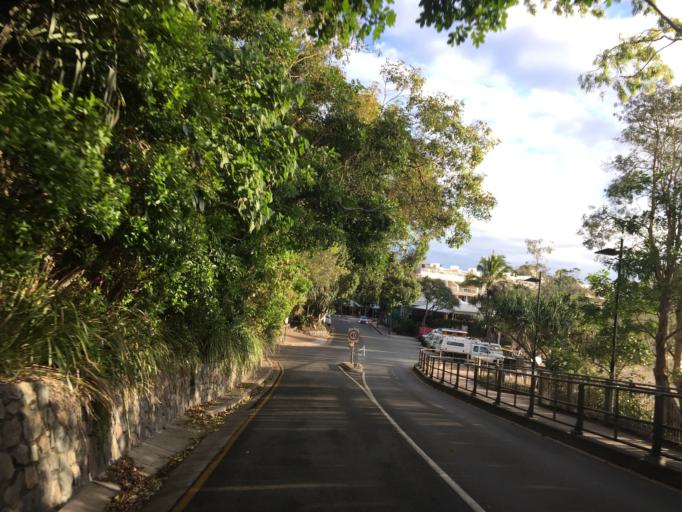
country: AU
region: Queensland
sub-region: Sunshine Coast
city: Noosa Heads
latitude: -26.3862
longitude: 153.0938
